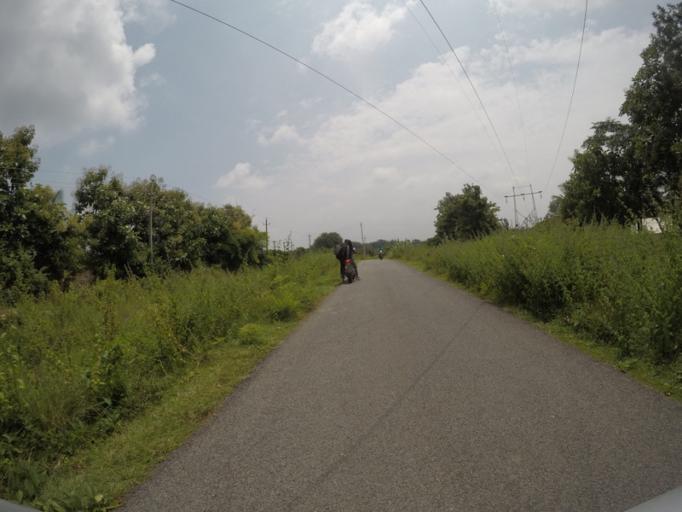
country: IN
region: Karnataka
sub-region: Ramanagara
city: Kanakapura
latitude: 12.6195
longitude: 77.4313
